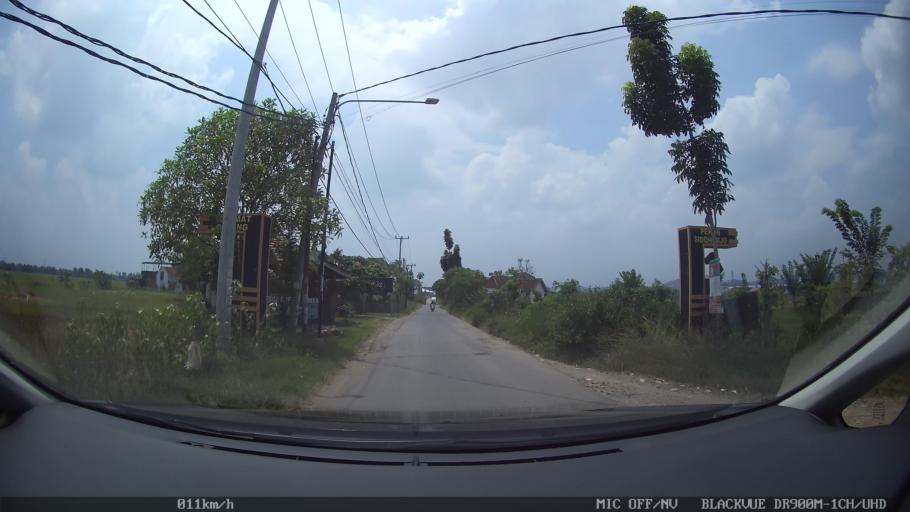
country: ID
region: Lampung
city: Pringsewu
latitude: -5.3529
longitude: 104.9909
